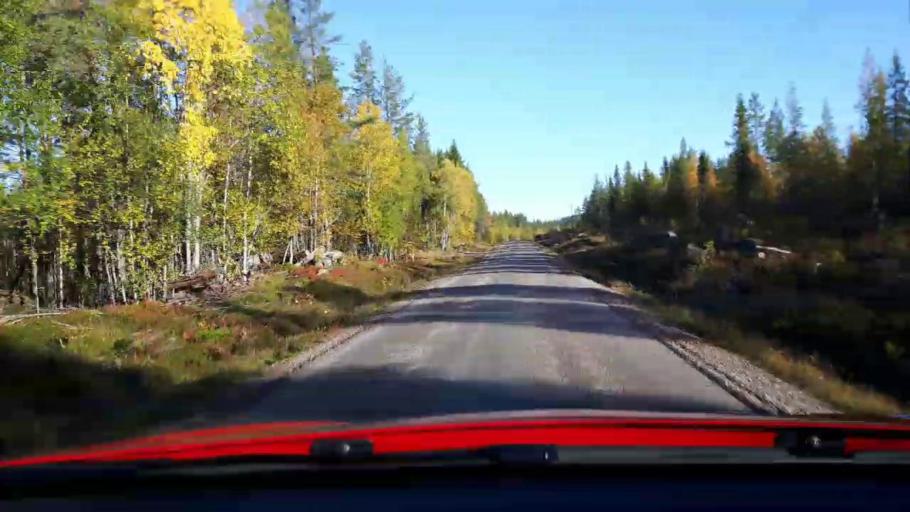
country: SE
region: Jaemtland
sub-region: Stroemsunds Kommun
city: Stroemsund
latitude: 64.3885
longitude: 15.1510
